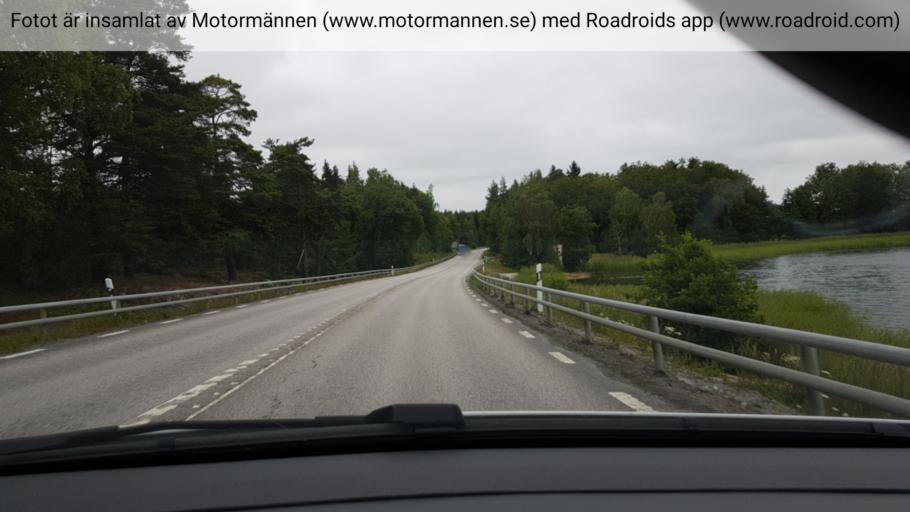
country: SE
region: Stockholm
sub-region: Lidingo
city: Brevik
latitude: 59.4310
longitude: 18.2200
